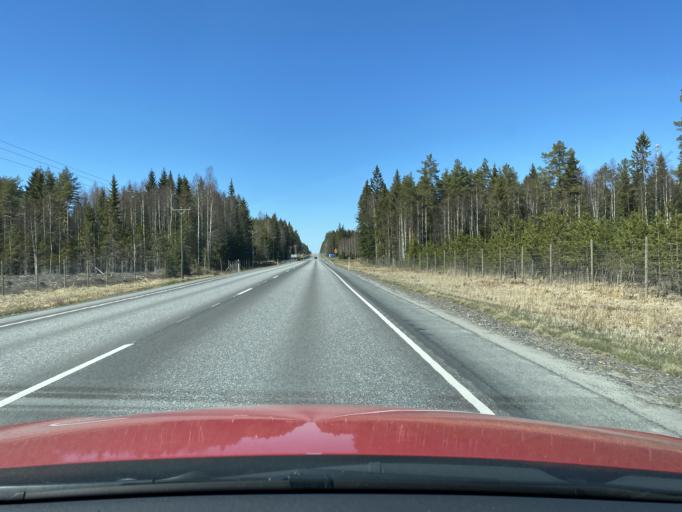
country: FI
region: Uusimaa
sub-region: Helsinki
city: Kaerkoelae
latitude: 60.6500
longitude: 23.8657
